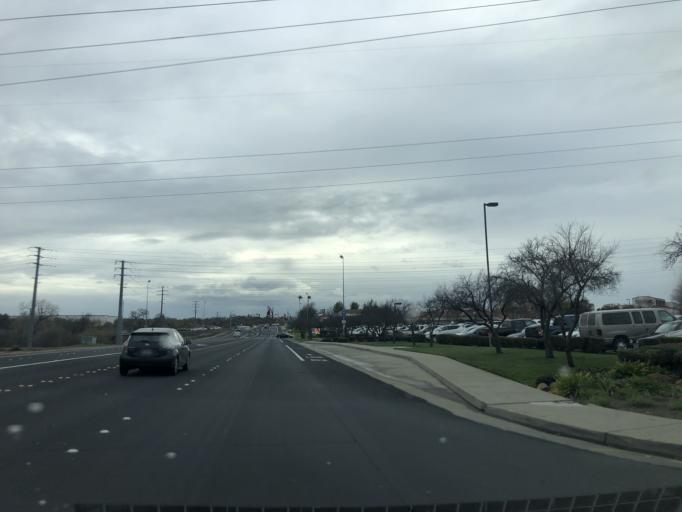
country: US
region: California
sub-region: Placer County
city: Roseville
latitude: 38.7602
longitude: -121.2572
